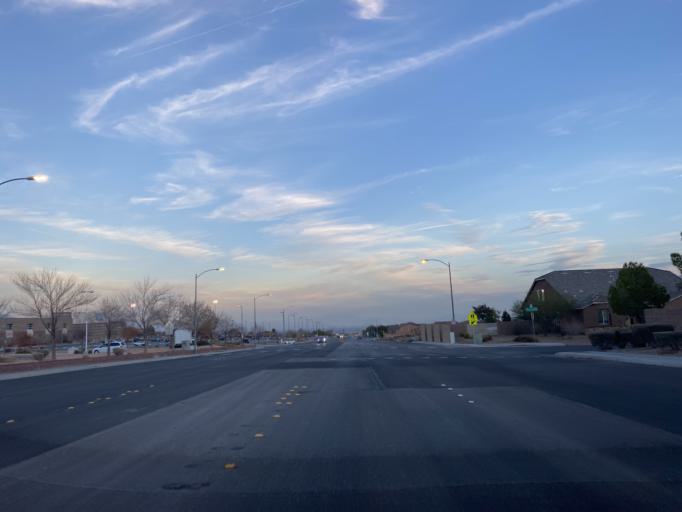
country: US
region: Nevada
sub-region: Clark County
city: Summerlin South
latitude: 36.2772
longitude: -115.3224
